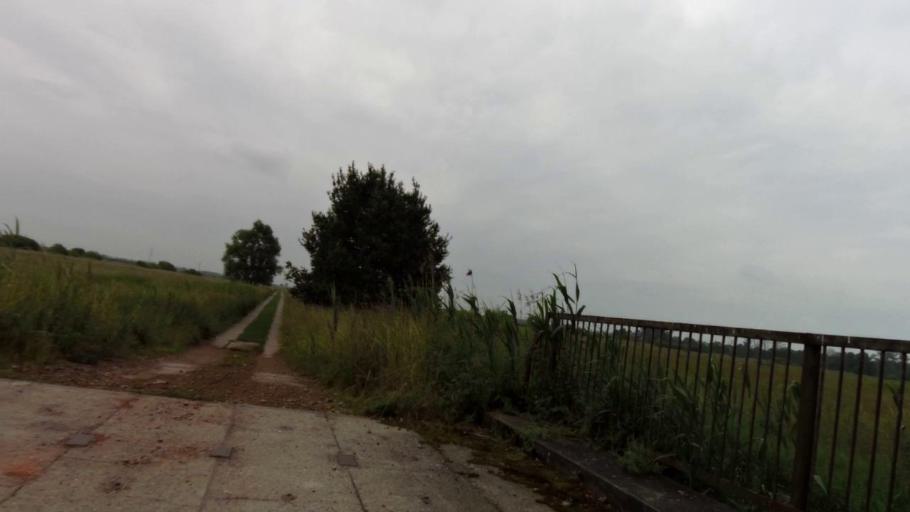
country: PL
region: West Pomeranian Voivodeship
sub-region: Powiat goleniowski
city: Stepnica
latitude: 53.5736
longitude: 14.6942
